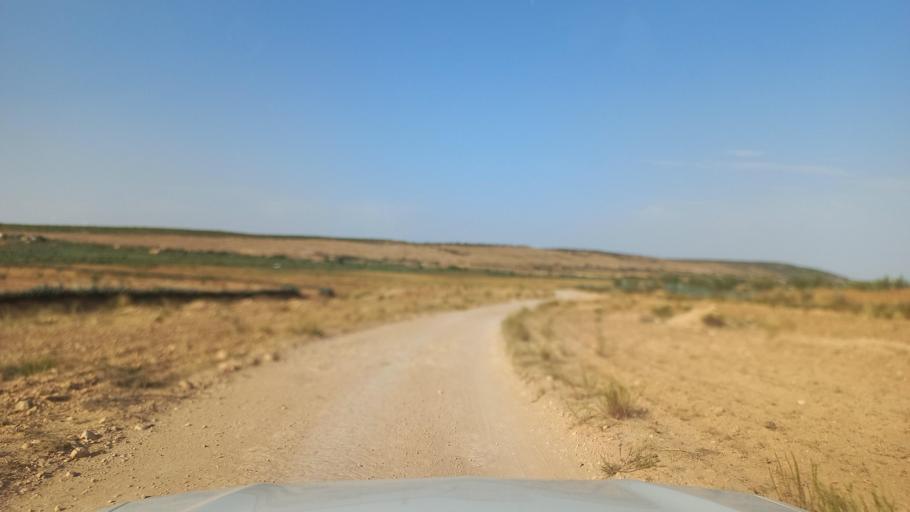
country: TN
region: Al Qasrayn
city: Kasserine
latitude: 35.3553
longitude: 8.8503
